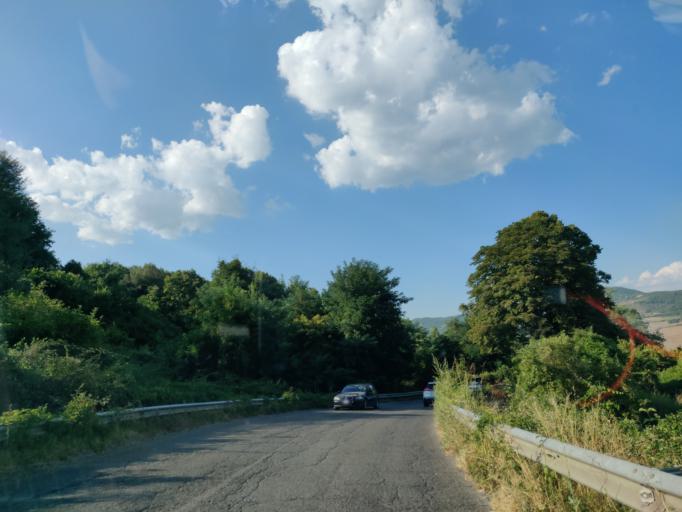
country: IT
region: Latium
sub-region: Provincia di Viterbo
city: Acquapendente
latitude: 42.7520
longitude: 11.8646
